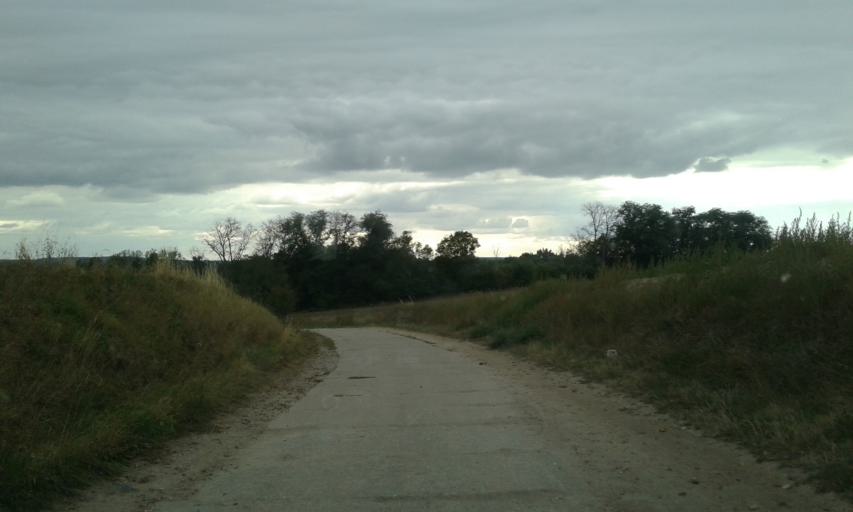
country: PL
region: West Pomeranian Voivodeship
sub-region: Powiat pyrzycki
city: Warnice
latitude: 53.1821
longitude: 15.0064
